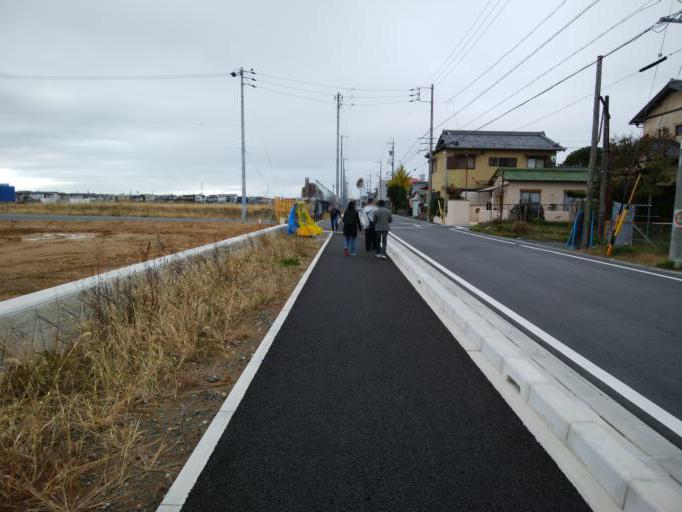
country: JP
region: Aichi
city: Toyohashi
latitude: 34.7309
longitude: 137.3873
